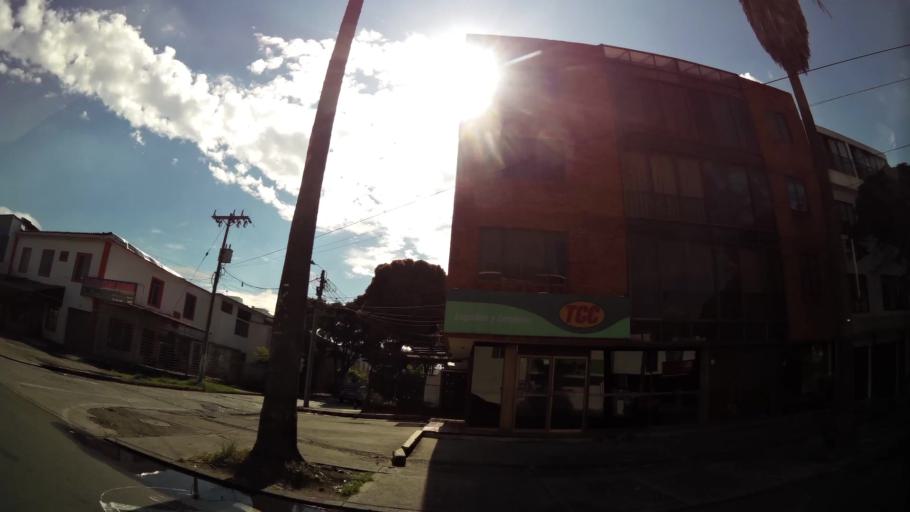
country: CO
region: Valle del Cauca
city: Cali
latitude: 3.4285
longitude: -76.5375
